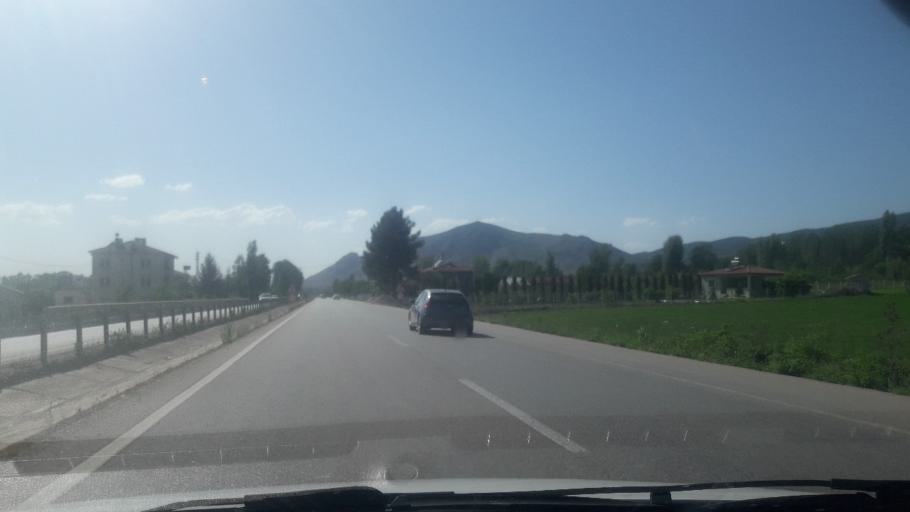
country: TR
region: Tokat
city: Dokmetepe
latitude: 40.3181
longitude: 36.2423
